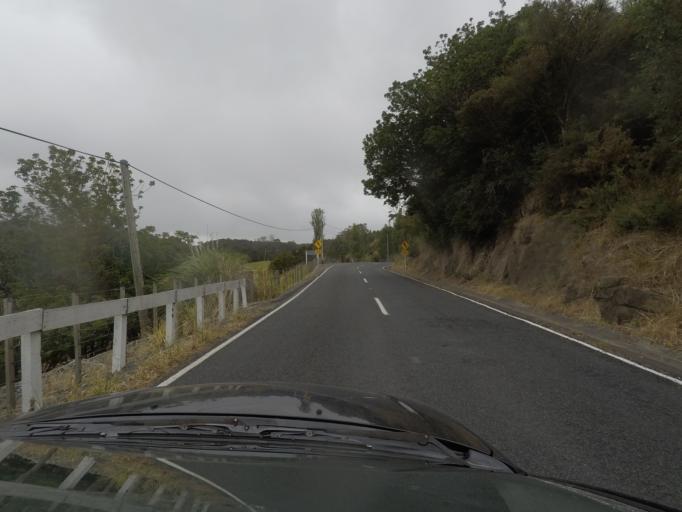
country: NZ
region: Auckland
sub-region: Auckland
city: Warkworth
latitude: -36.2762
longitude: 174.6978
